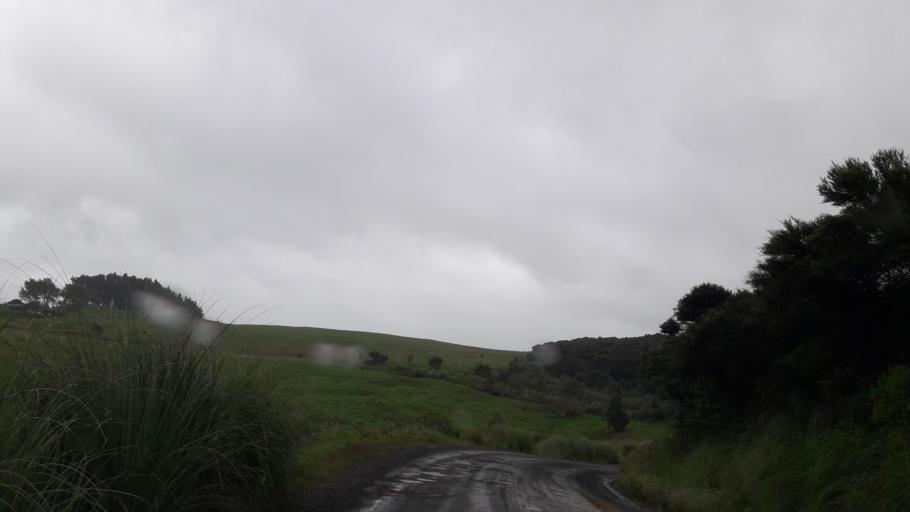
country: NZ
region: Northland
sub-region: Far North District
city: Kaitaia
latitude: -35.4065
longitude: 173.3649
